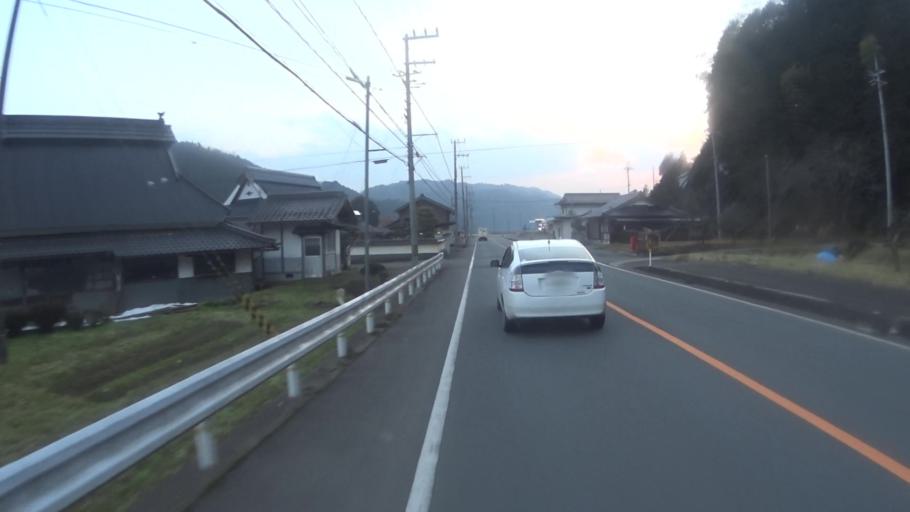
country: JP
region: Kyoto
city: Maizuru
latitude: 35.3507
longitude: 135.3797
